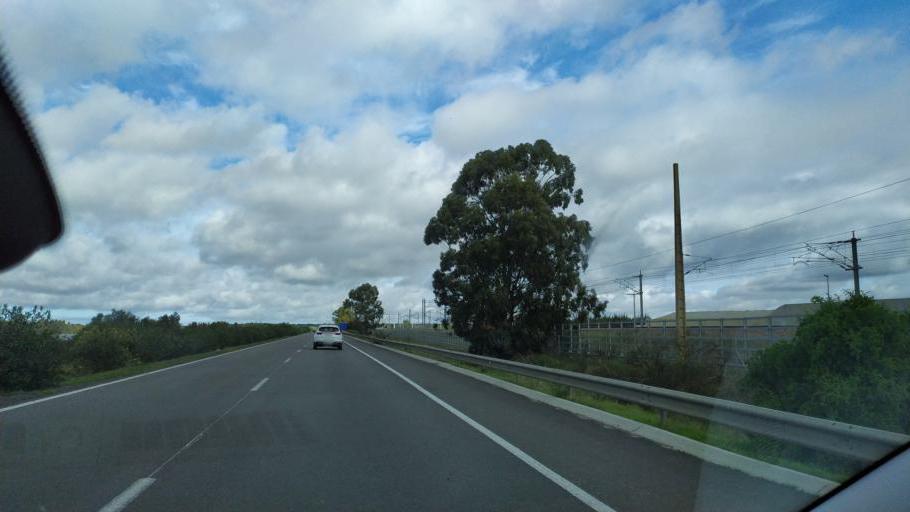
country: MA
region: Gharb-Chrarda-Beni Hssen
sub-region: Kenitra Province
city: Lalla Mimouna
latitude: 34.8876
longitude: -6.2102
